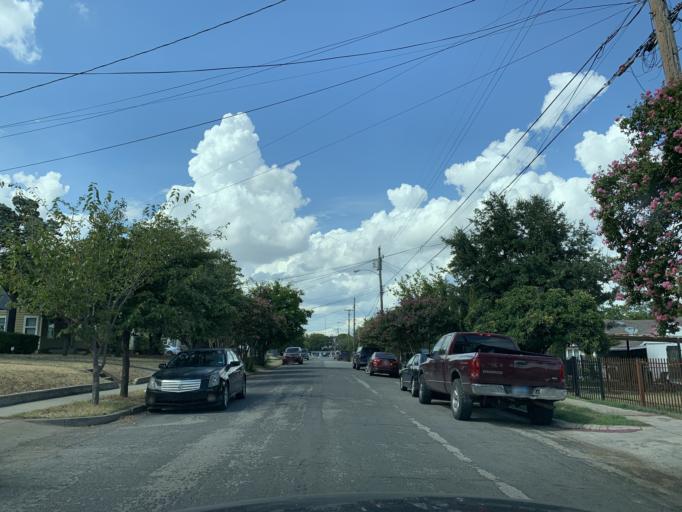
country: US
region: Texas
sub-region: Dallas County
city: Cockrell Hill
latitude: 32.7468
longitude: -96.8688
